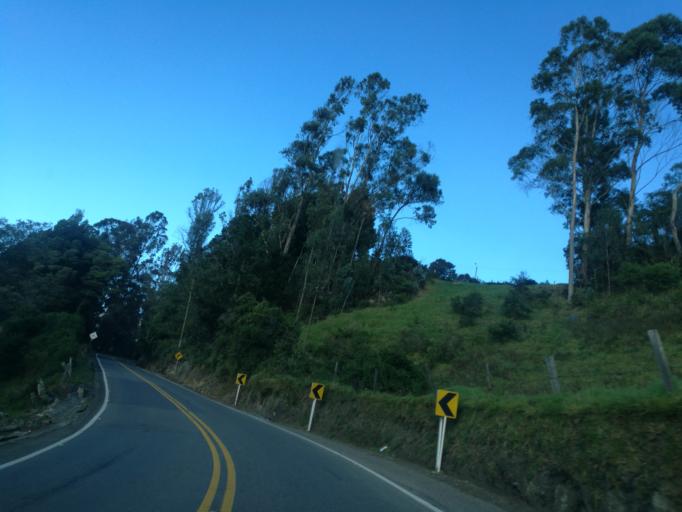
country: CO
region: Boyaca
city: Chiquinquira
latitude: 5.6229
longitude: -73.7543
